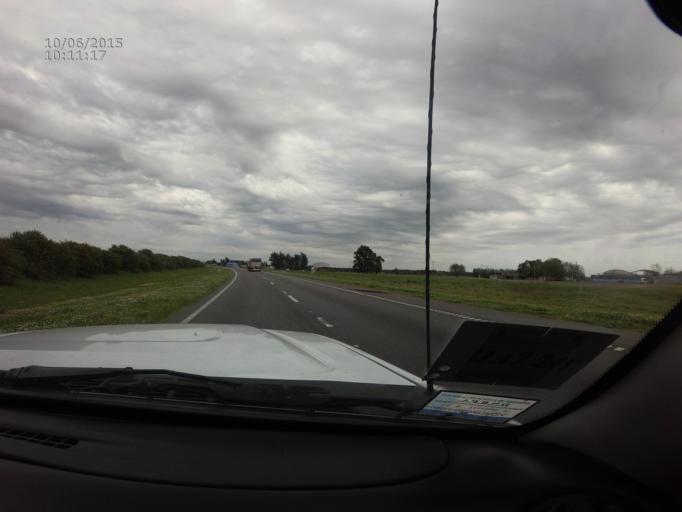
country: AR
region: Buenos Aires
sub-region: Partido de San Pedro
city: San Pedro
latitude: -33.7762
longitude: -59.6517
